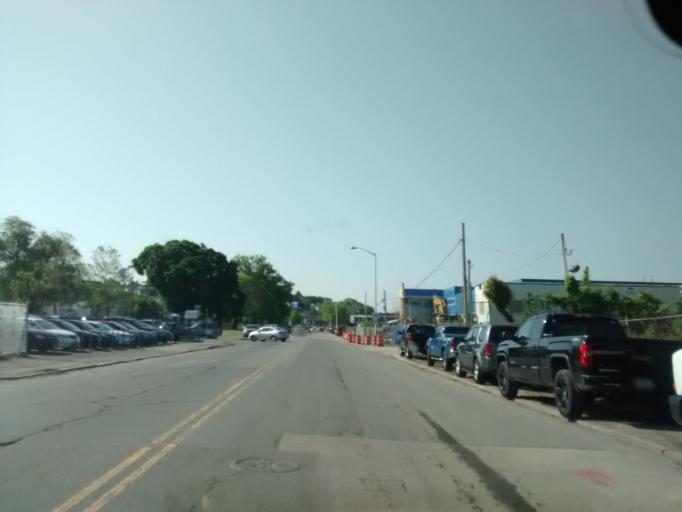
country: US
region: Massachusetts
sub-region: Worcester County
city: Worcester
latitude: 42.2512
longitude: -71.8053
